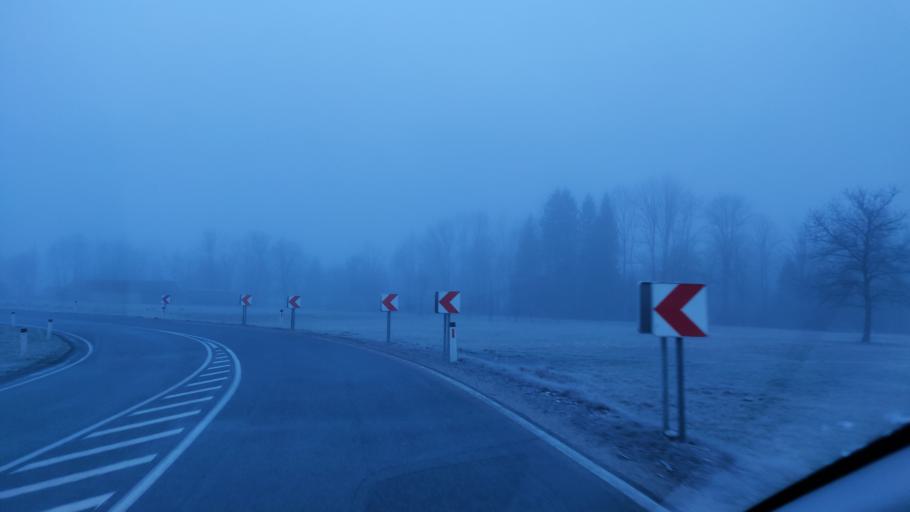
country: SI
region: Bohinj
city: Bohinjska Bistrica
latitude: 46.2774
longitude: 13.9507
